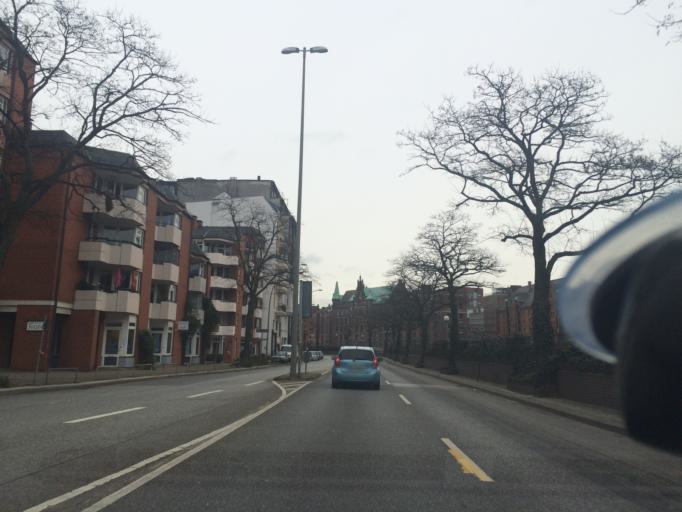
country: DE
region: Hamburg
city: Neustadt
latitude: 53.5448
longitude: 9.9904
